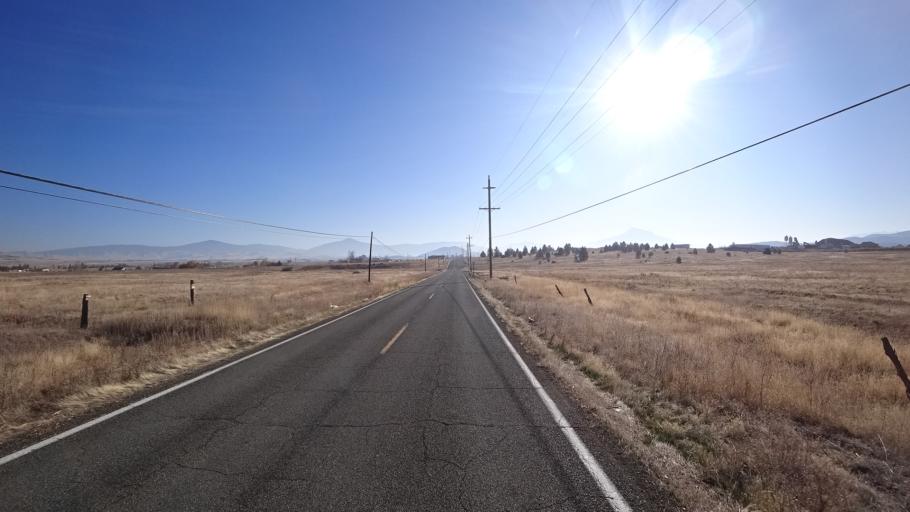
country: US
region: California
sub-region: Siskiyou County
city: Yreka
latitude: 41.7368
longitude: -122.5995
